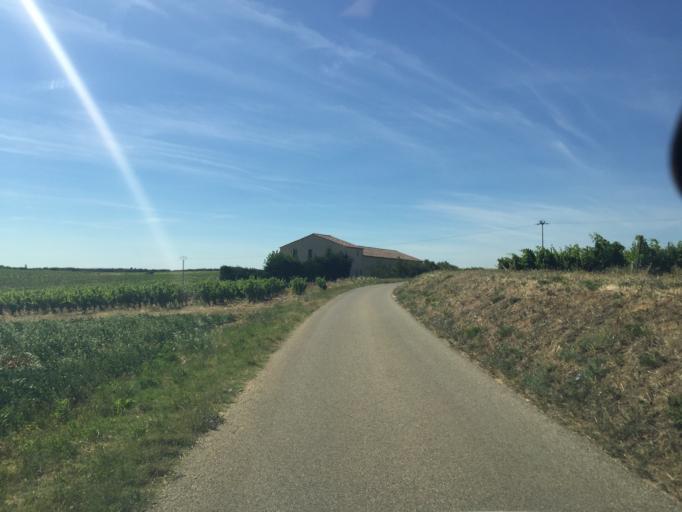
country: FR
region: Provence-Alpes-Cote d'Azur
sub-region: Departement du Vaucluse
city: Chateauneuf-du-Pape
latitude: 44.0623
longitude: 4.8121
